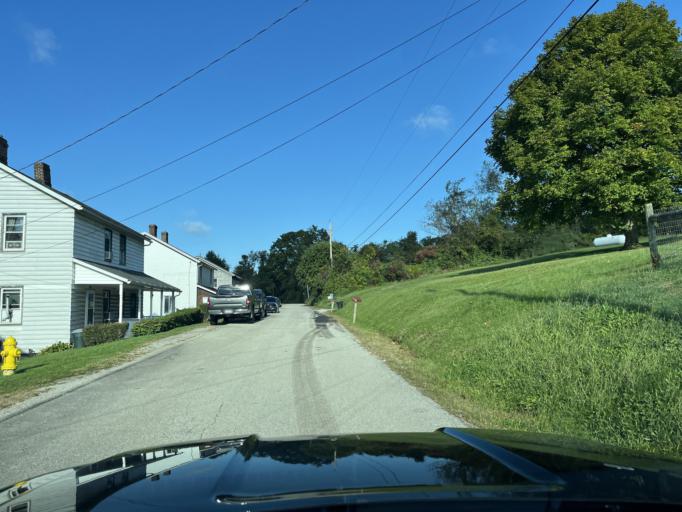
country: US
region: Pennsylvania
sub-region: Fayette County
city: South Uniontown
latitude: 39.8795
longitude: -79.7706
